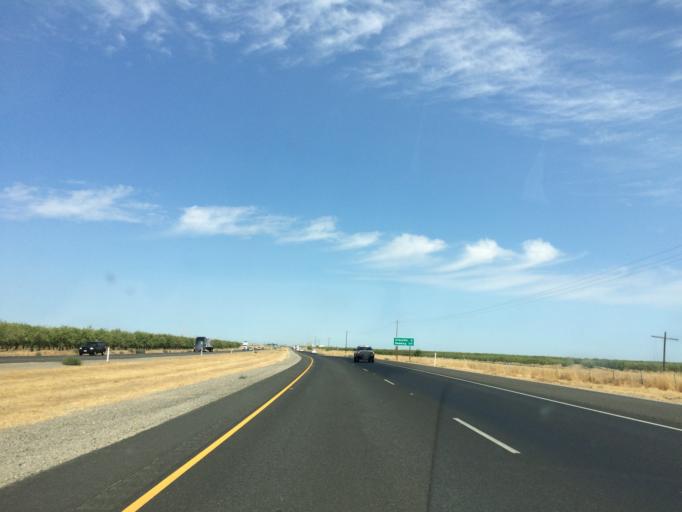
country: US
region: California
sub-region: Yolo County
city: Dunnigan
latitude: 38.9357
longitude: -122.0036
